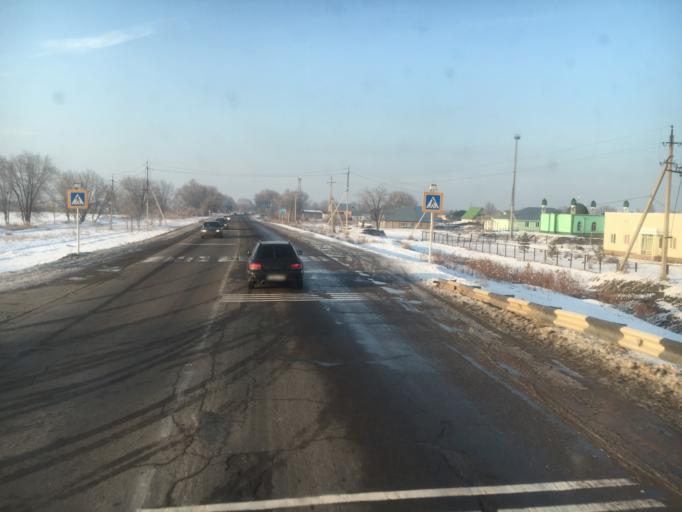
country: KZ
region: Almaty Oblysy
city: Burunday
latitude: 43.3324
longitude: 76.6616
